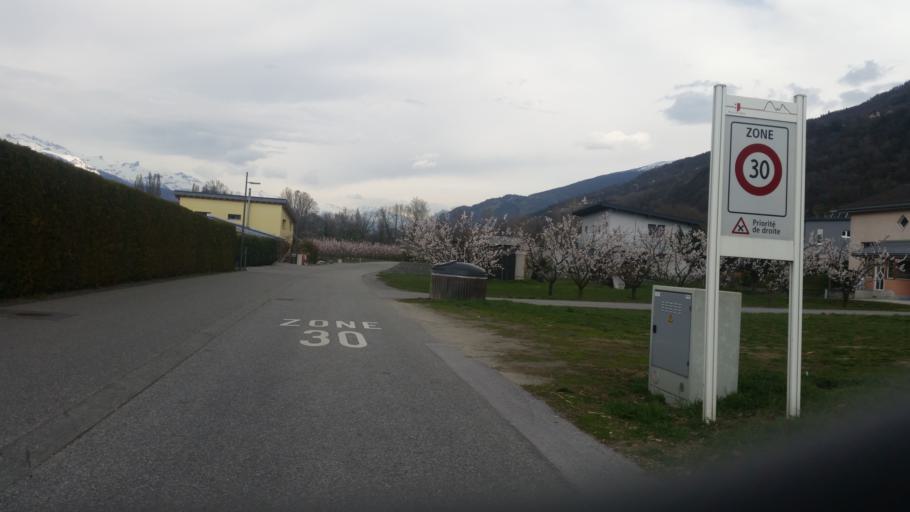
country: CH
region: Valais
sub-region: Conthey District
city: Basse-Nendaz
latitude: 46.2074
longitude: 7.3155
